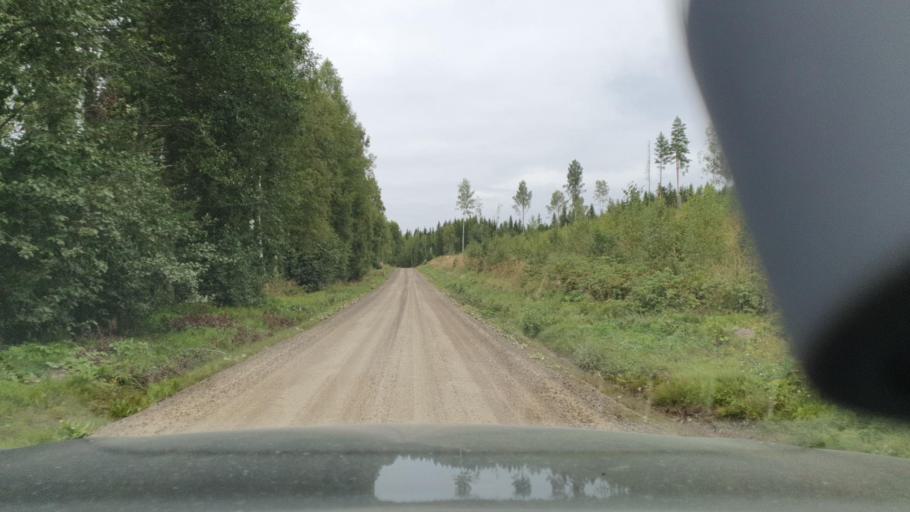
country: SE
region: Vaermland
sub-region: Arvika Kommun
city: Arvika
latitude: 59.9416
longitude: 12.6603
